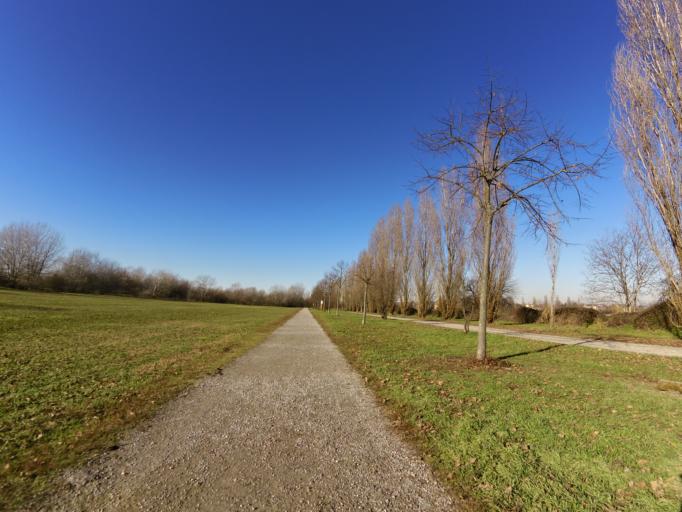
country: IT
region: Lombardy
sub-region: Citta metropolitana di Milano
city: Chiaravalle
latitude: 45.4256
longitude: 9.2257
